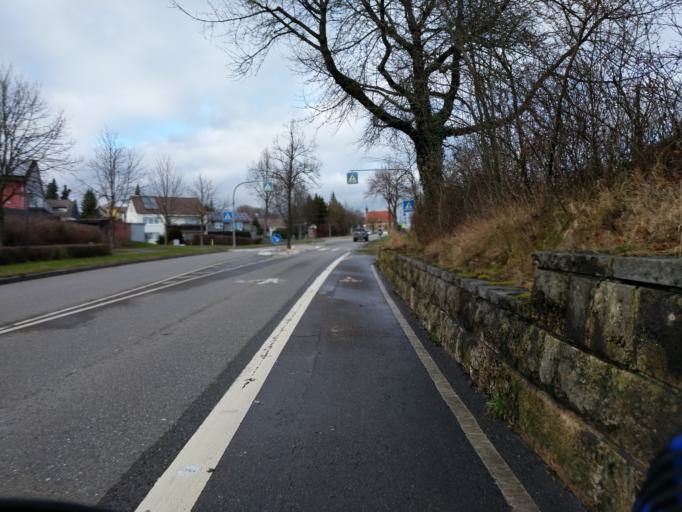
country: DE
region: Baden-Wuerttemberg
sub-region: Tuebingen Region
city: Rottenburg
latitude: 48.4838
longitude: 8.9360
